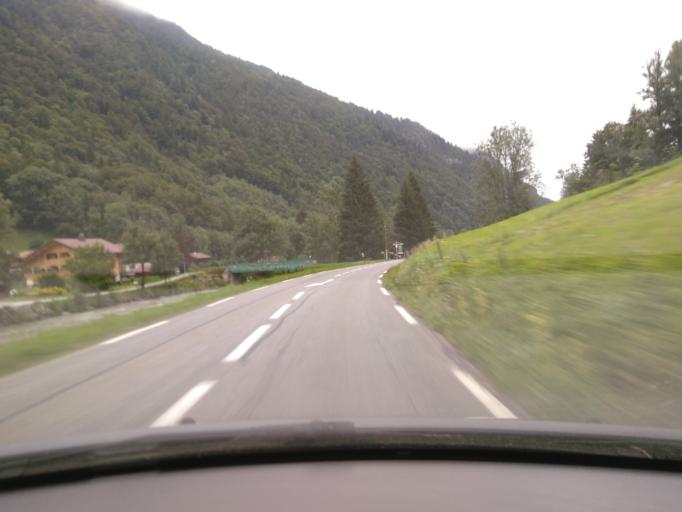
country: FR
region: Rhone-Alpes
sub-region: Departement de la Haute-Savoie
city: Saint-Jean-de-Sixt
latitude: 45.9655
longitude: 6.3856
